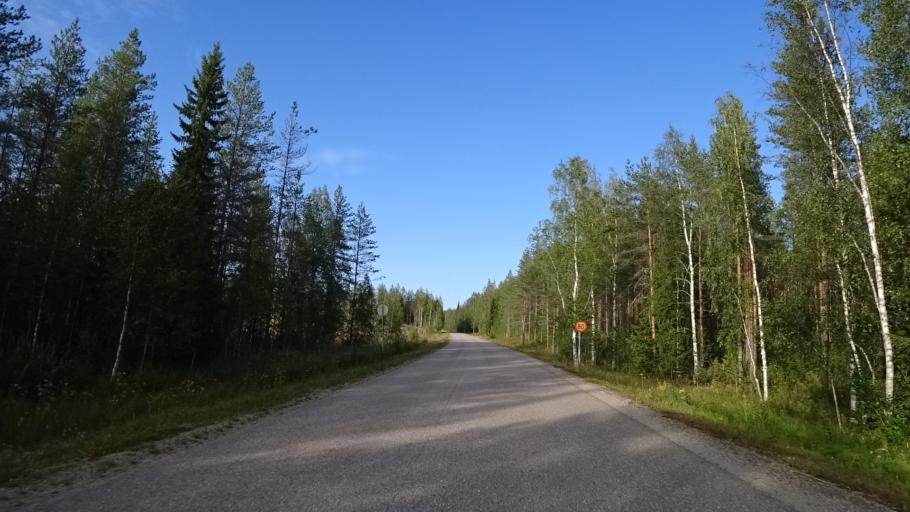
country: FI
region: North Karelia
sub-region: Joensuu
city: Eno
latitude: 63.0300
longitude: 30.5244
